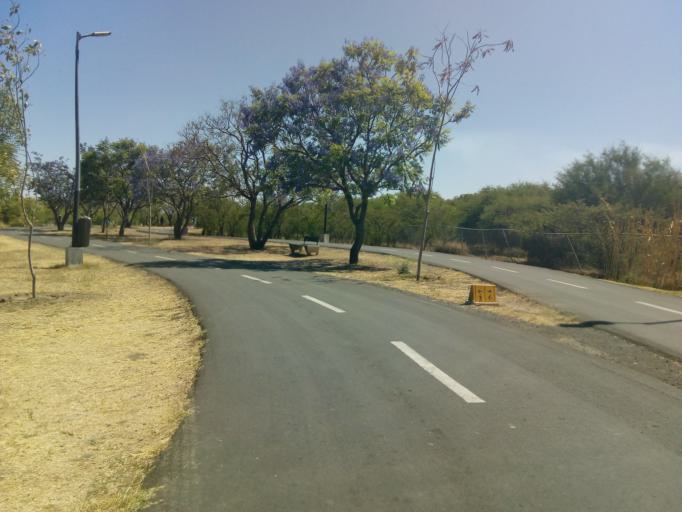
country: MX
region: Guanajuato
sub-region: Leon
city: La Ermita
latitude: 21.1832
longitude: -101.6958
